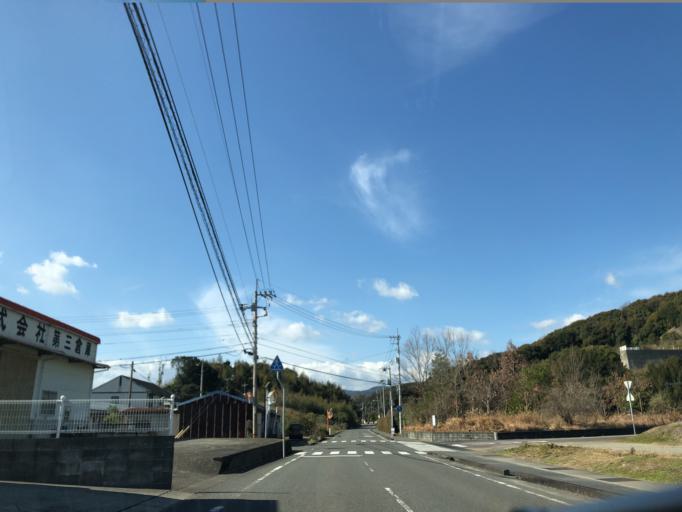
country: JP
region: Kochi
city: Sukumo
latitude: 32.9271
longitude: 132.6822
